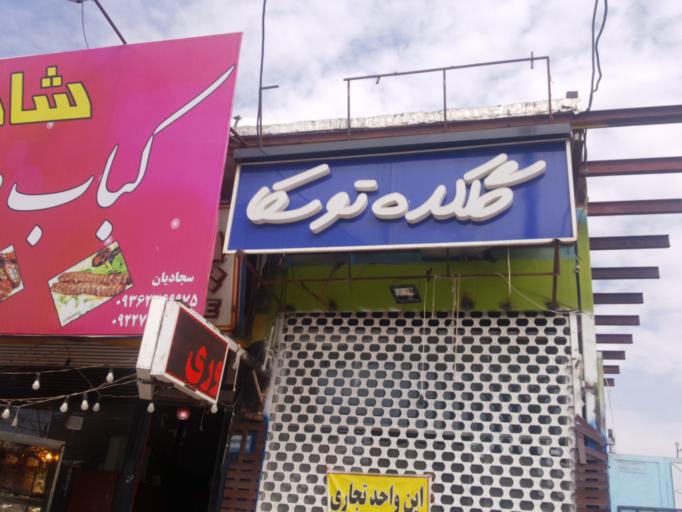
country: IR
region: Fars
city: Marvdasht
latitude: 29.8801
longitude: 52.8081
